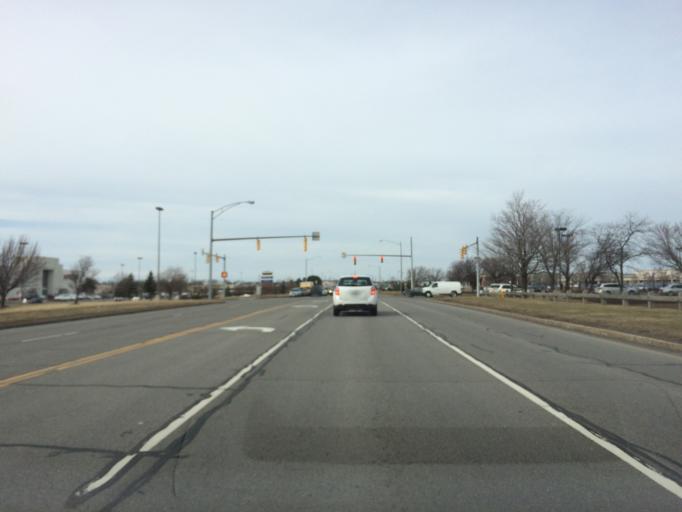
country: US
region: New York
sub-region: Monroe County
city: Rochester
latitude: 43.0823
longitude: -77.6296
